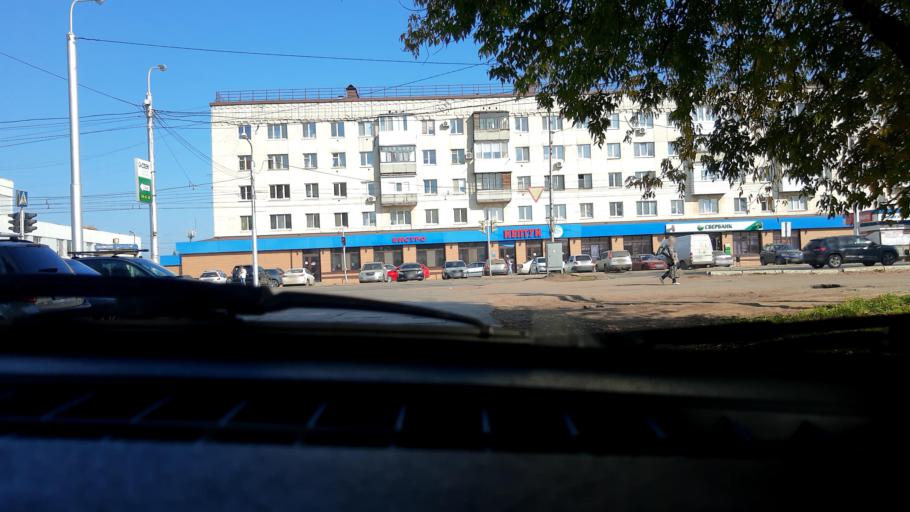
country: RU
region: Bashkortostan
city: Mikhaylovka
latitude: 54.7893
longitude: 55.8804
